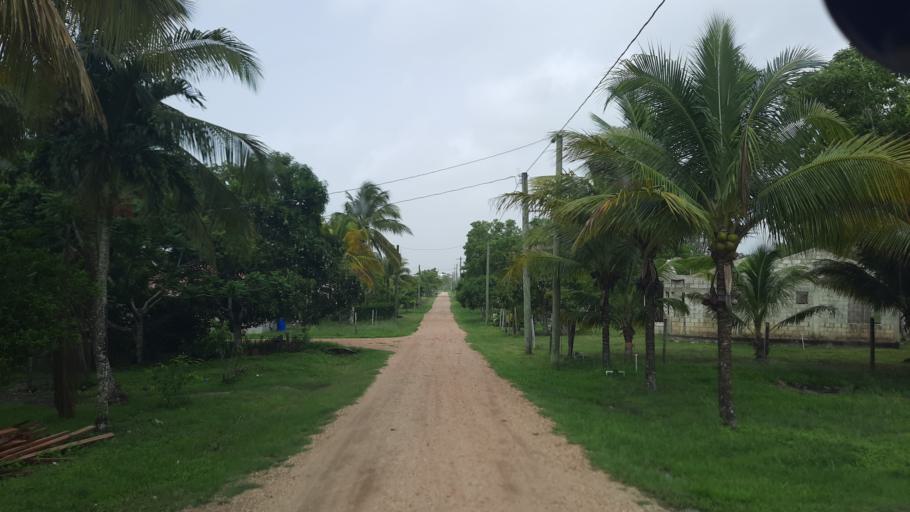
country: BZ
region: Cayo
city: Valley of Peace
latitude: 17.2523
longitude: -88.9390
